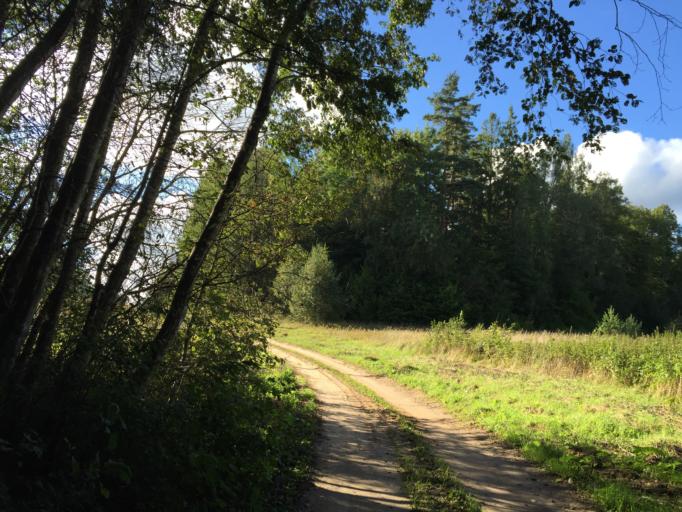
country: LV
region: Kuldigas Rajons
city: Kuldiga
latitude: 57.0080
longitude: 21.7835
